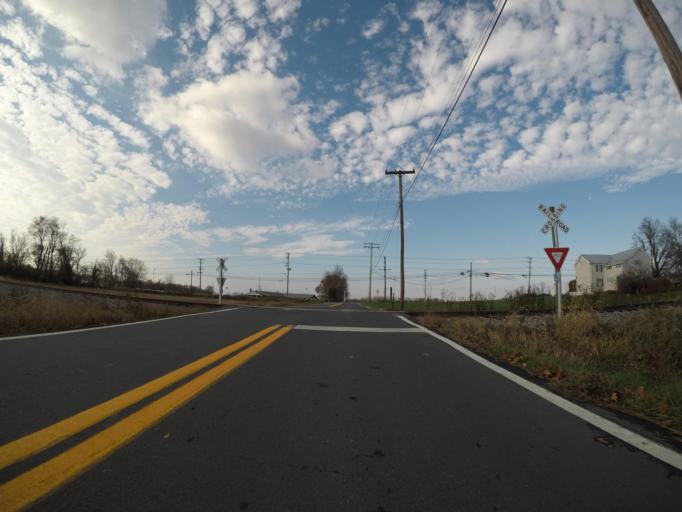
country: US
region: Maryland
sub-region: Carroll County
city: Hampstead
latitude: 39.5857
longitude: -76.8415
